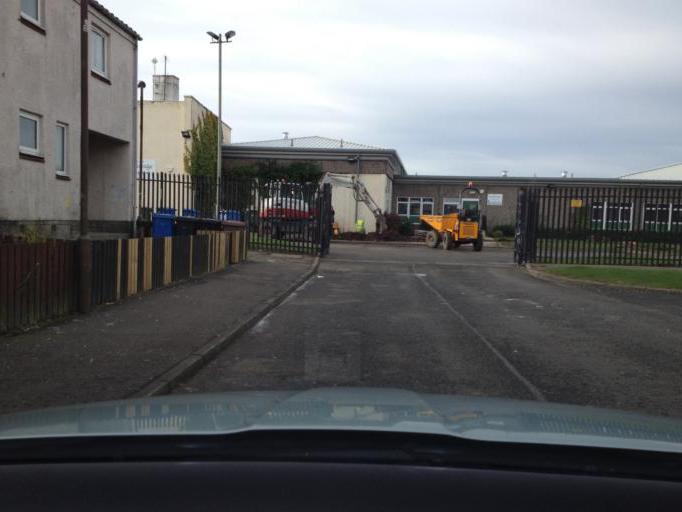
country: GB
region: Scotland
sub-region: West Lothian
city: Livingston
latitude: 55.9086
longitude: -3.5210
